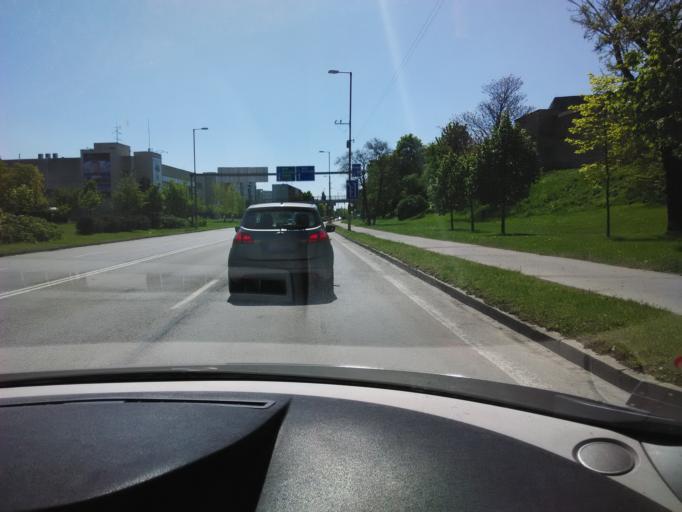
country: SK
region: Trnavsky
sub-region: Okres Trnava
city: Trnava
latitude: 48.3810
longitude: 17.5922
